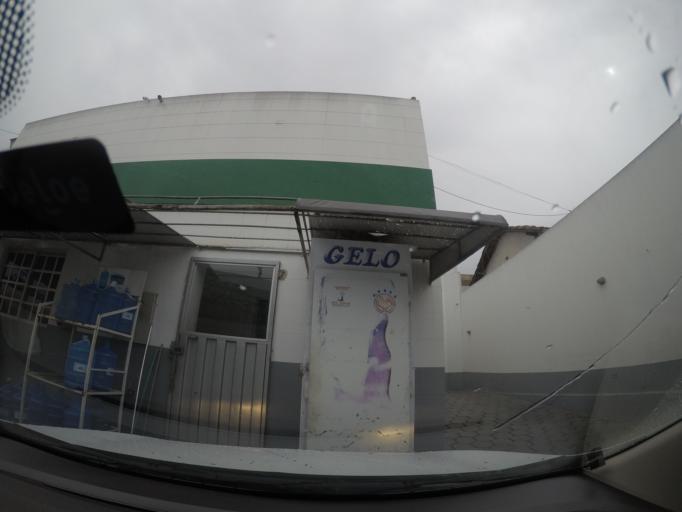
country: BR
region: Goias
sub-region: Goiania
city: Goiania
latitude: -16.6841
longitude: -49.2501
